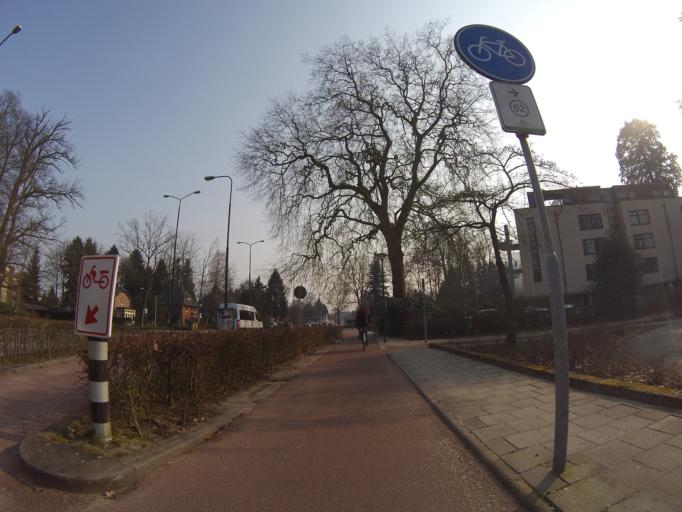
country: NL
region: Utrecht
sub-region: Gemeente Soest
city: Soest
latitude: 52.1914
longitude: 5.2820
